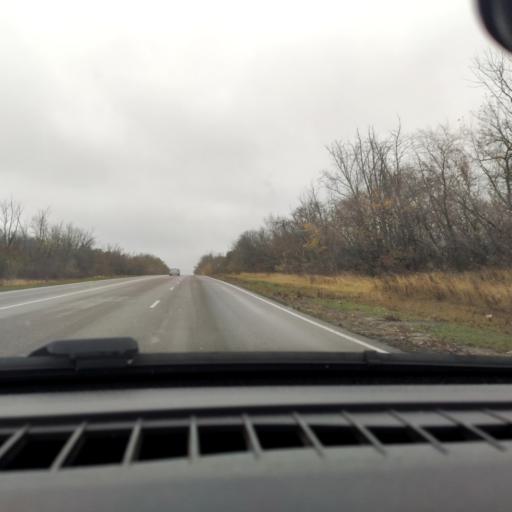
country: RU
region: Voronezj
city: Uryv-Pokrovka
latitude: 51.1398
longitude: 39.0544
